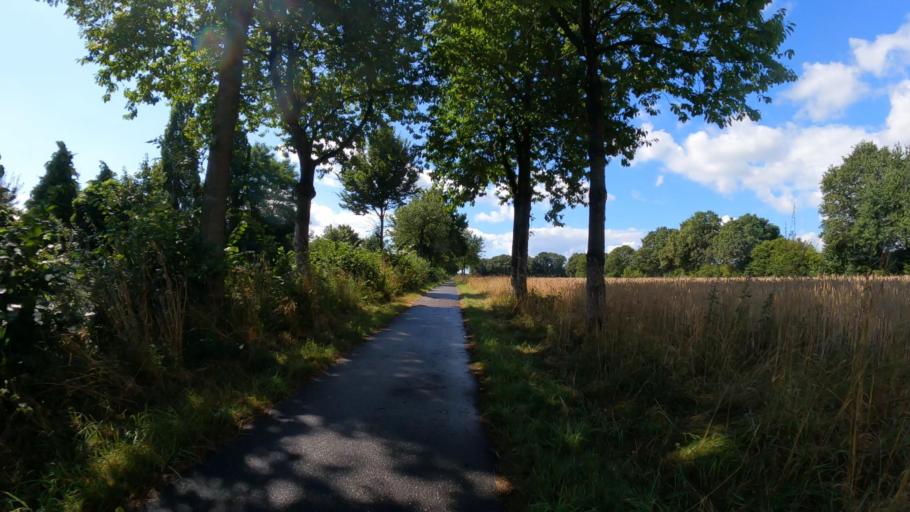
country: DE
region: Schleswig-Holstein
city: Fuhlendorf
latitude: 53.9377
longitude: 9.8935
